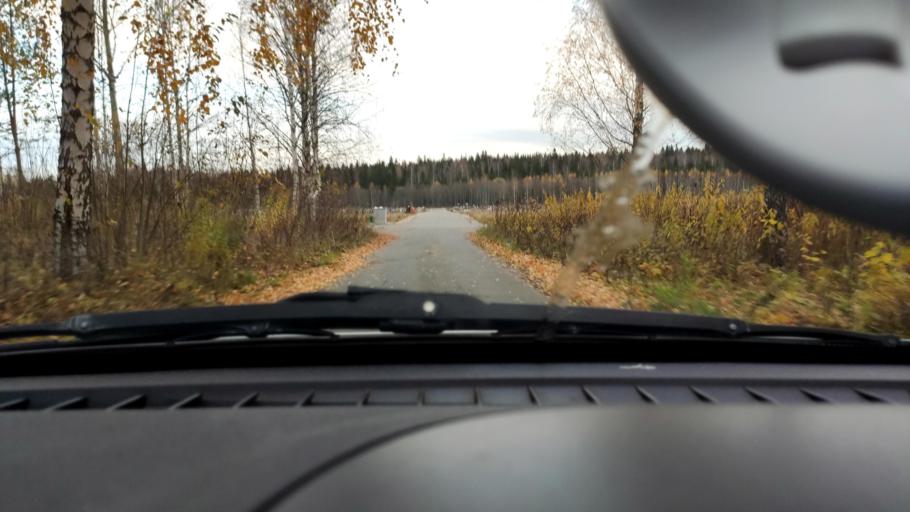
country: RU
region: Perm
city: Kondratovo
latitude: 58.0684
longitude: 56.1357
